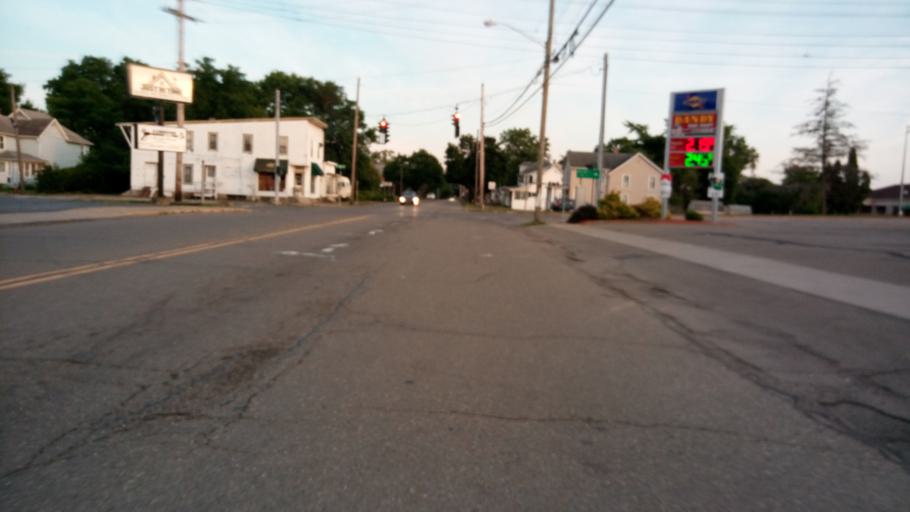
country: US
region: New York
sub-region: Chemung County
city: Elmira Heights
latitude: 42.1303
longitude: -76.8184
